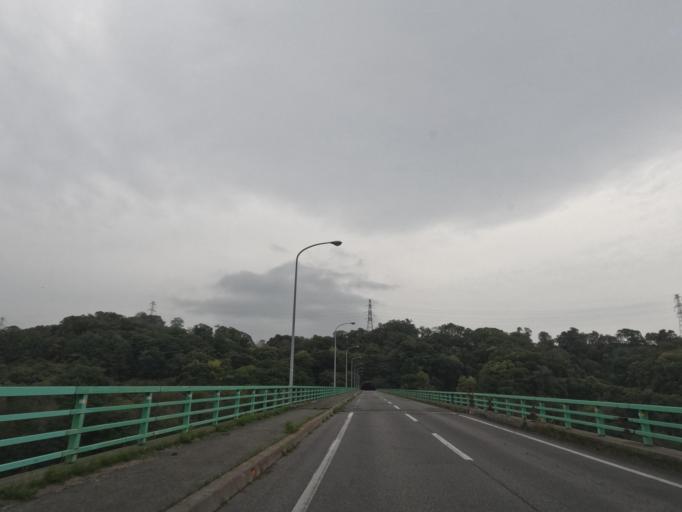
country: JP
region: Hokkaido
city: Date
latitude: 42.5082
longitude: 140.8624
